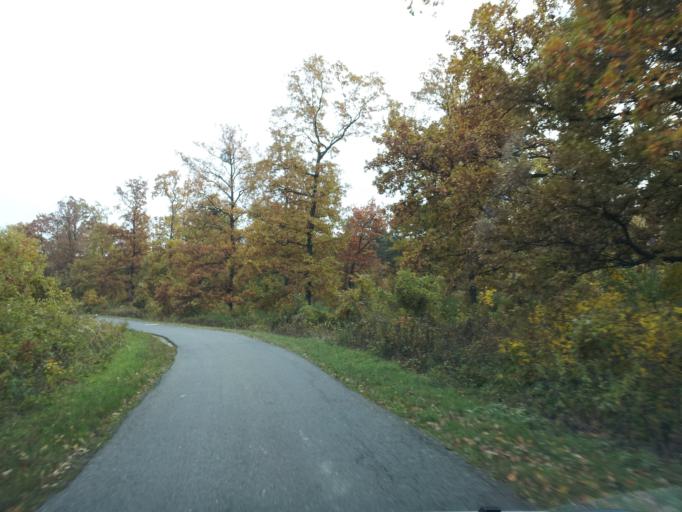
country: HU
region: Gyor-Moson-Sopron
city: Pannonhalma
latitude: 47.4973
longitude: 17.7405
